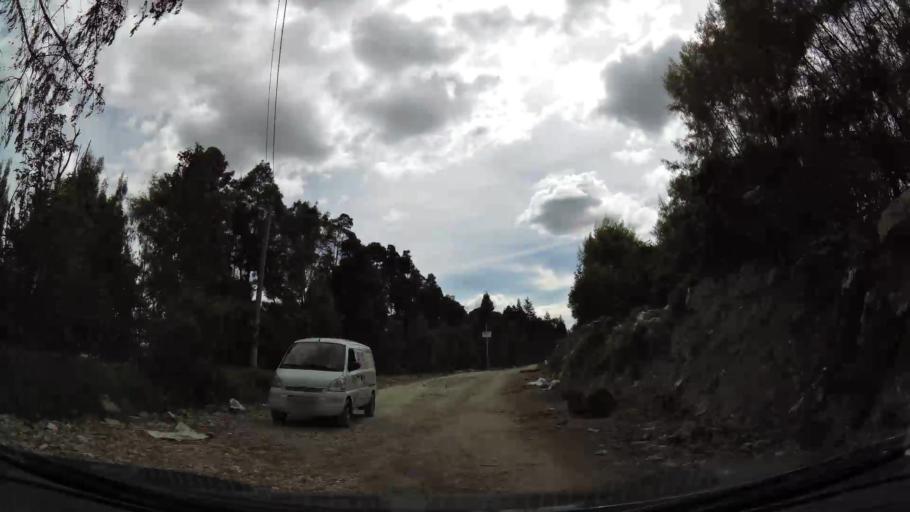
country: CO
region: Cundinamarca
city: Funza
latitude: 4.7329
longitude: -74.1495
